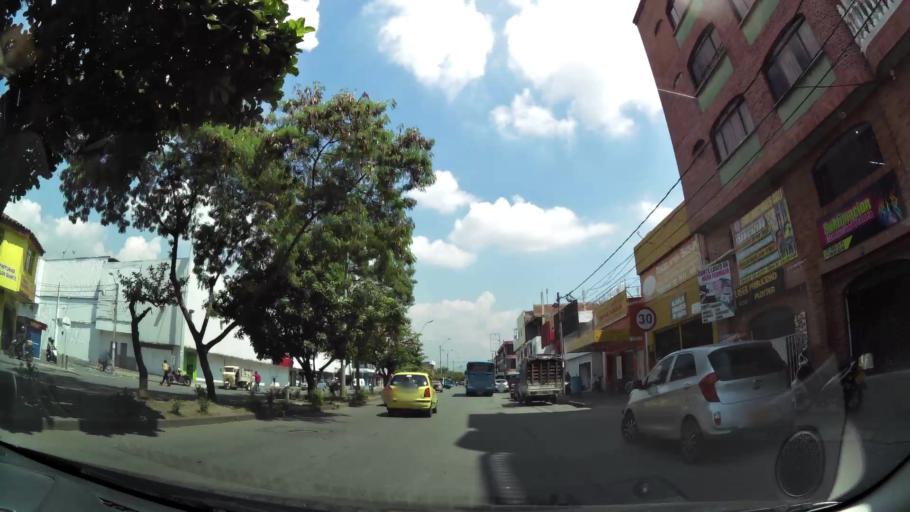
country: CO
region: Valle del Cauca
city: Cali
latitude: 3.4392
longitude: -76.5260
